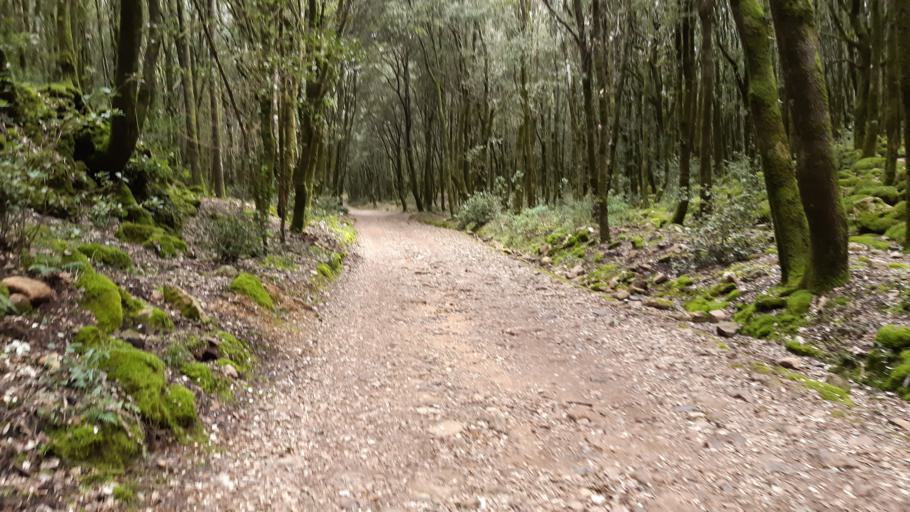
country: IT
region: Sardinia
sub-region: Provincia di Carbonia-Iglesias
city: Iglesias
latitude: 39.3848
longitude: 8.5760
